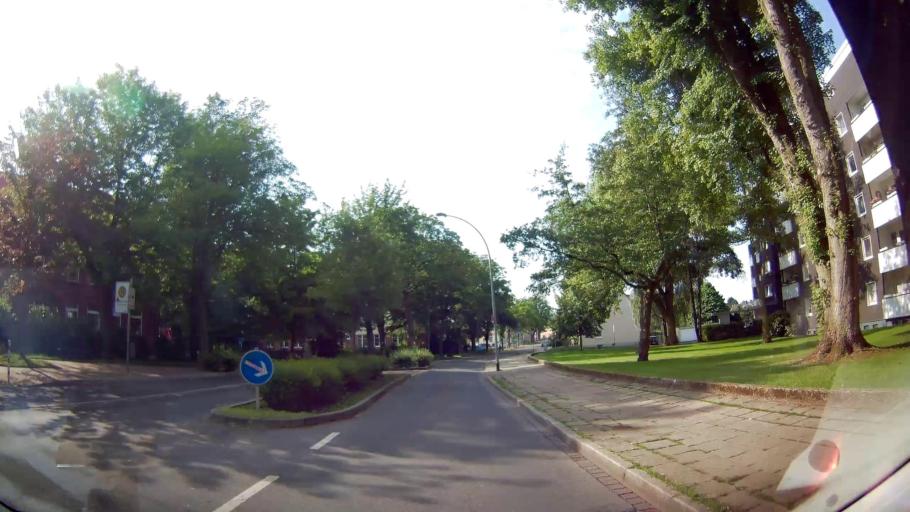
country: DE
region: North Rhine-Westphalia
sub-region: Regierungsbezirk Arnsberg
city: Herne
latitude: 51.5279
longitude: 7.2300
